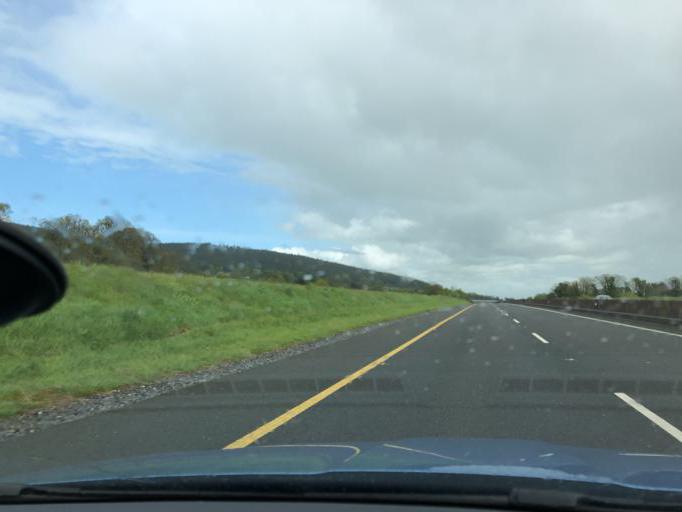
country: IE
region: Munster
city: Cahir
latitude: 52.3729
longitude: -7.9589
